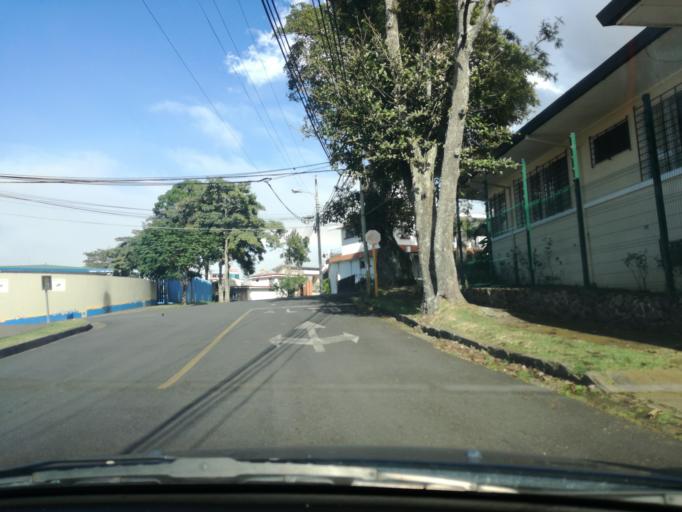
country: CR
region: San Jose
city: San Pedro
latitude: 9.9271
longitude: -84.0522
